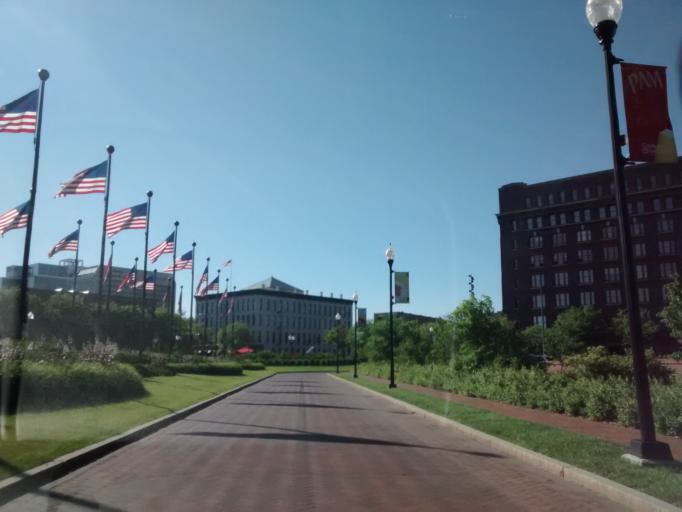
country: US
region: Nebraska
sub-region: Douglas County
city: Omaha
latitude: 41.2567
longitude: -95.9279
